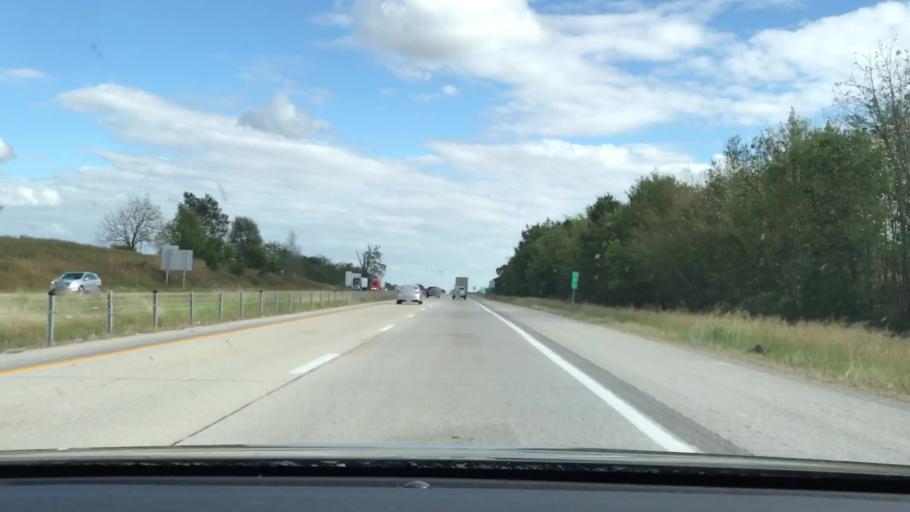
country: US
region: Kentucky
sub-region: Trigg County
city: Cadiz
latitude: 36.8765
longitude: -87.7265
